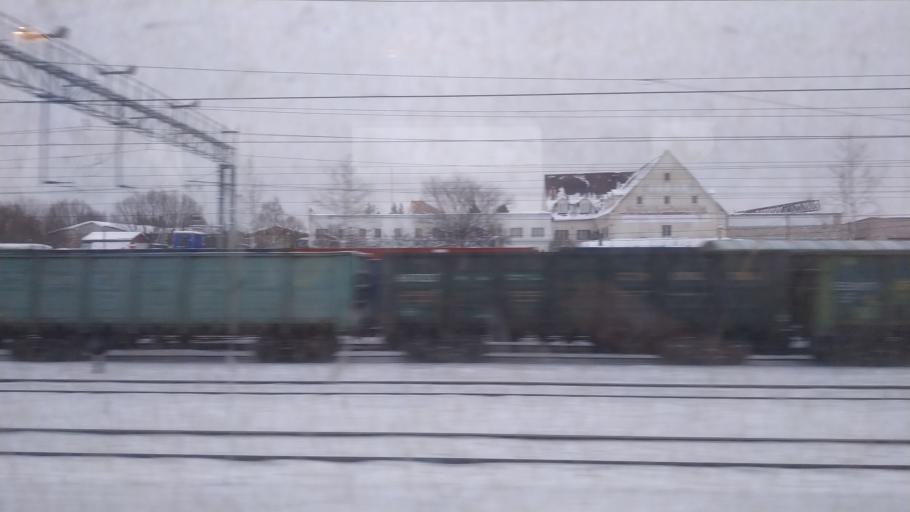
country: RU
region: Moskovskaya
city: Shcherbinka
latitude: 55.4791
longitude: 37.5545
